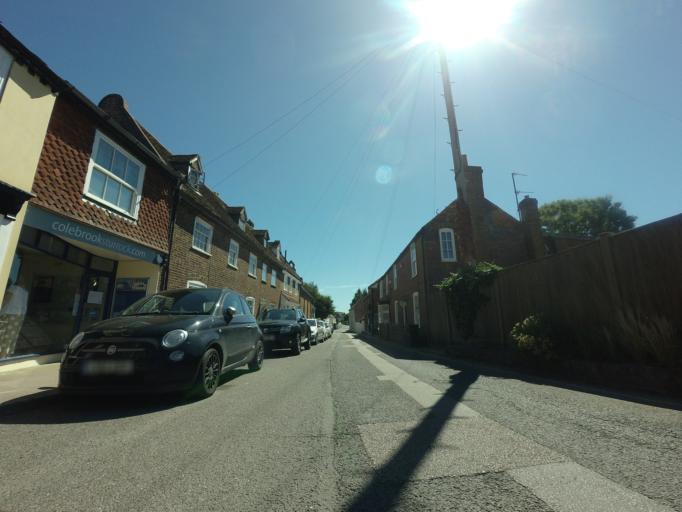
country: GB
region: England
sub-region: Kent
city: Ash
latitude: 51.2787
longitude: 1.2802
